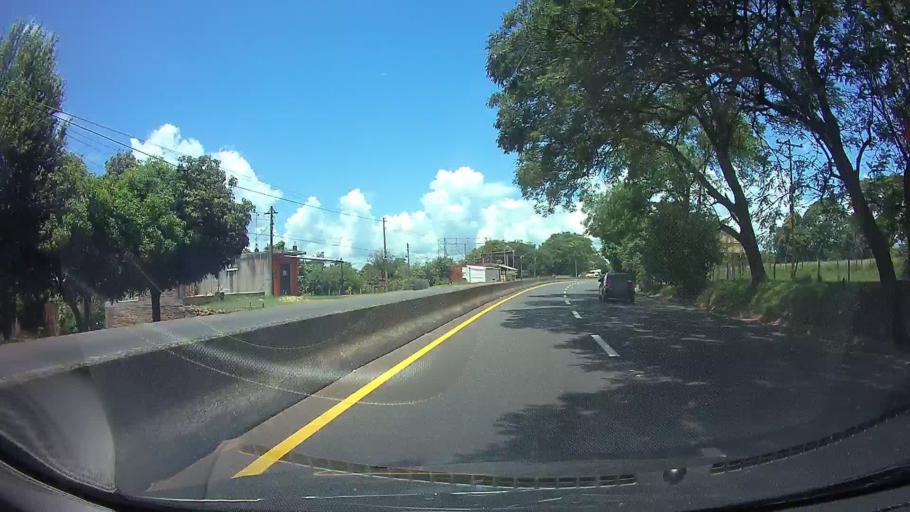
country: PY
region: Central
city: Itaugua
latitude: -25.3791
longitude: -57.3821
